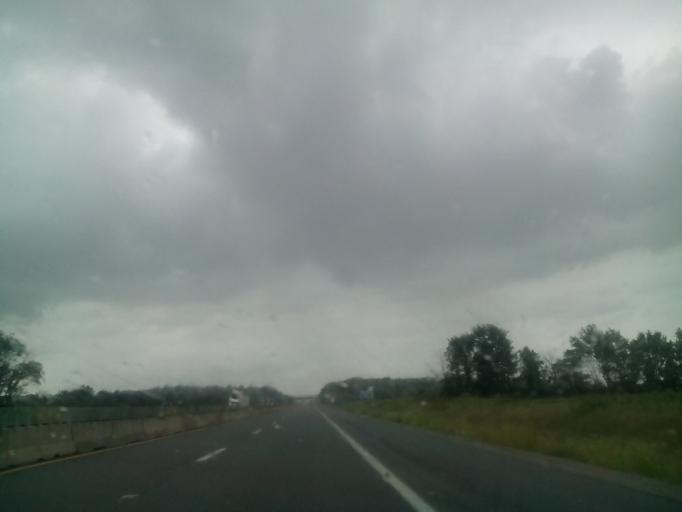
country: US
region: Ohio
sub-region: Sandusky County
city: Clyde
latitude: 41.3608
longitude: -82.9227
